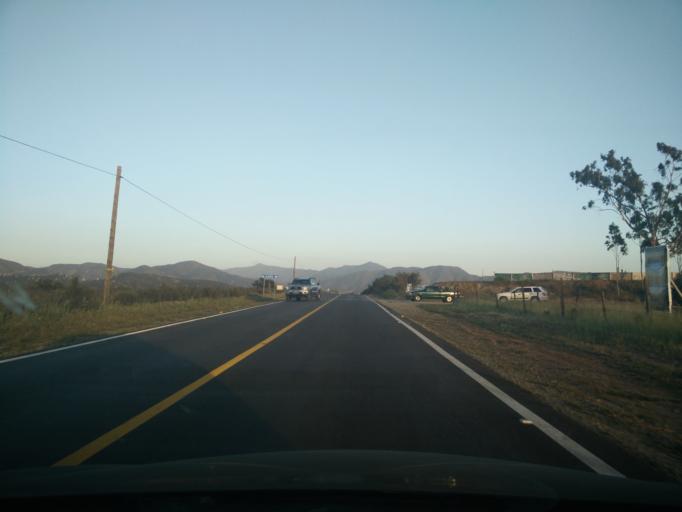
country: MX
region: Baja California
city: El Sauzal
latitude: 32.0030
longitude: -116.6701
